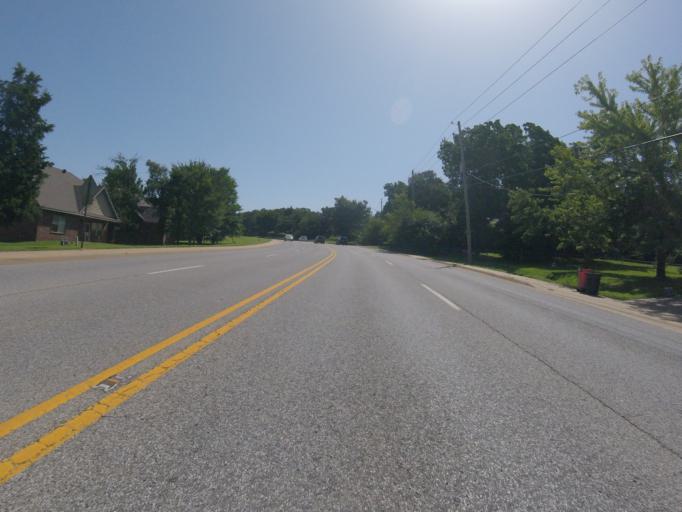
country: US
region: Arkansas
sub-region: Washington County
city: Fayetteville
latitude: 36.0779
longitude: -94.1859
